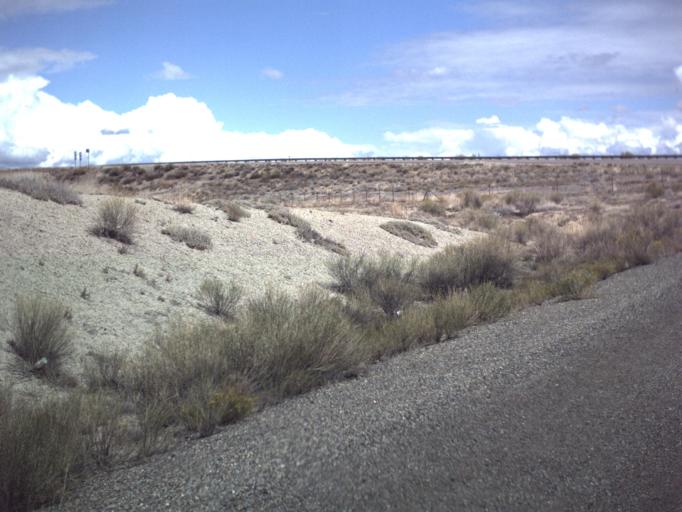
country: US
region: Colorado
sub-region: Mesa County
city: Loma
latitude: 39.1109
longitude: -109.1836
